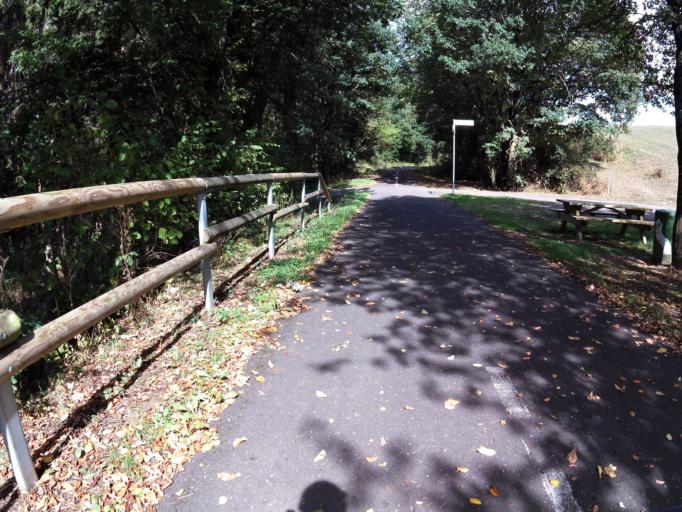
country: DE
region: Rheinland-Pfalz
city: Kickeshausen
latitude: 50.0722
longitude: 6.2566
